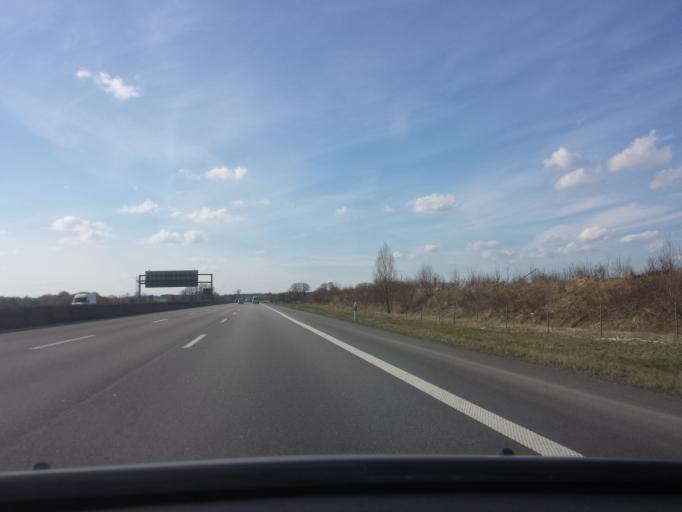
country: DE
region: Bavaria
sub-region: Upper Bavaria
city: Bergkirchen
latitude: 48.2408
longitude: 11.3342
